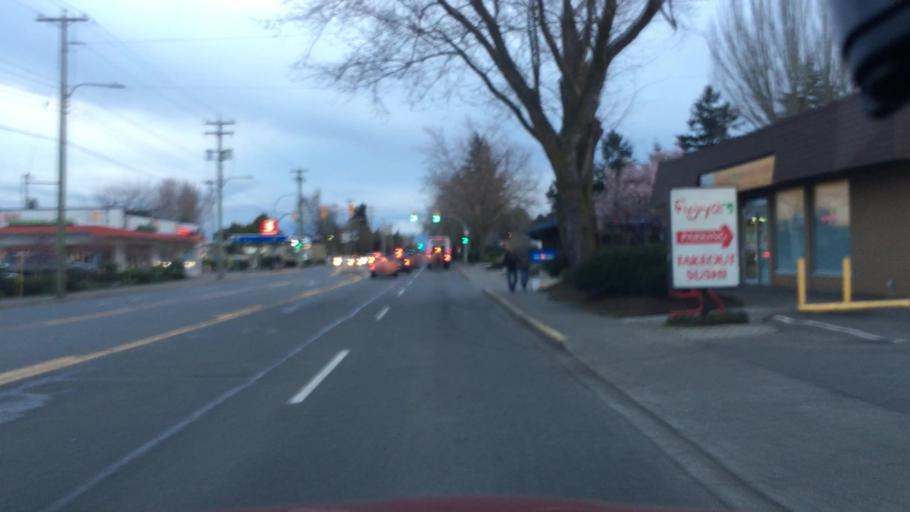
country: CA
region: British Columbia
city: Oak Bay
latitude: 48.4596
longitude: -123.3331
